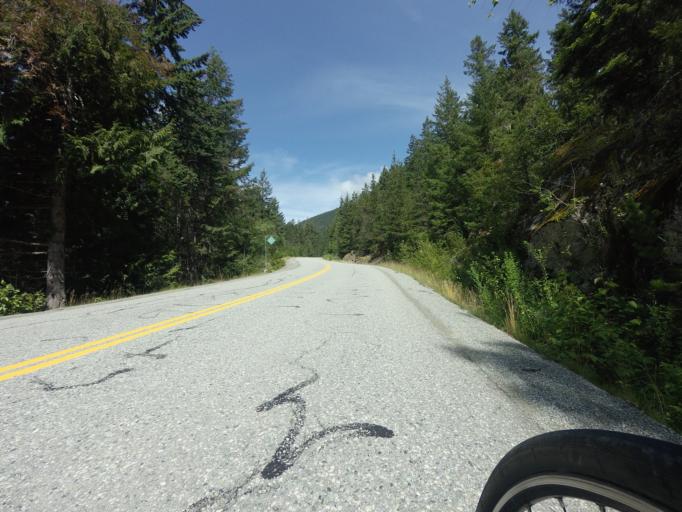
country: CA
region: British Columbia
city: Pemberton
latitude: 50.3037
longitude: -122.5745
